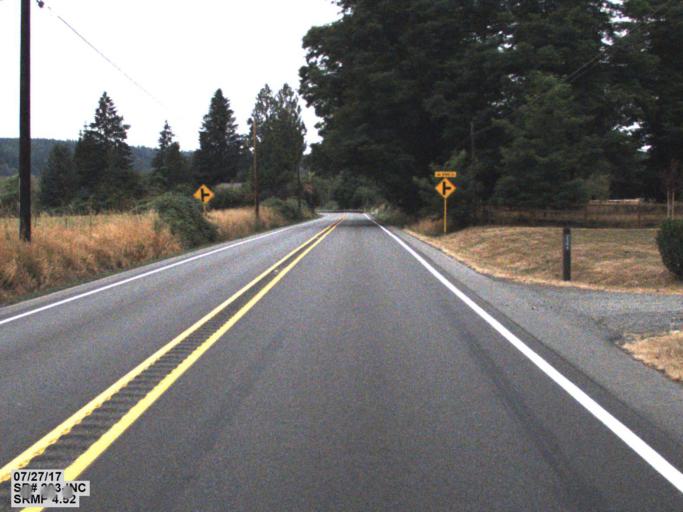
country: US
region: Washington
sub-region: King County
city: Carnation
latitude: 47.6279
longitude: -121.9110
